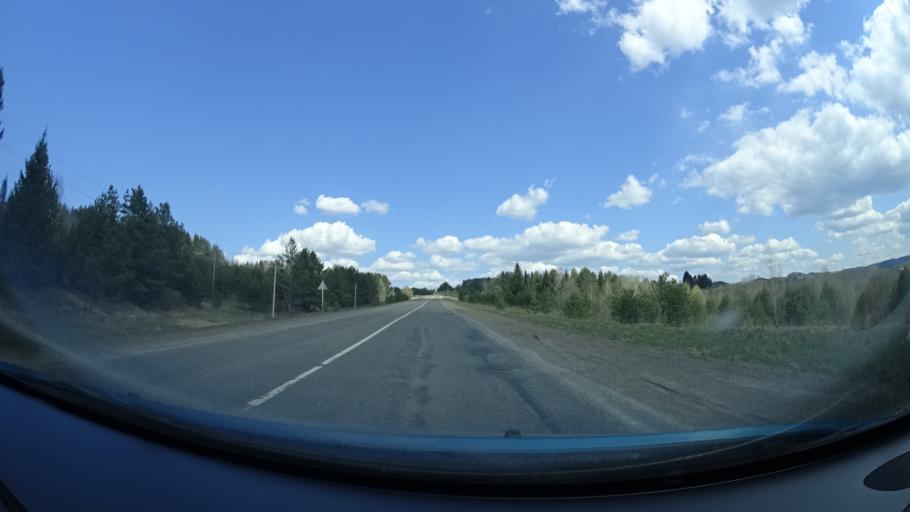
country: RU
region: Perm
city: Osa
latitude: 57.2277
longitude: 55.5893
